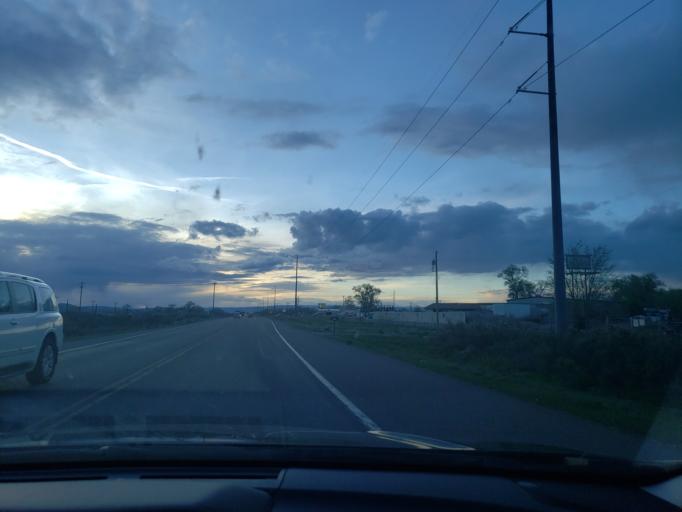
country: US
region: Colorado
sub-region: Mesa County
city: Redlands
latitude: 39.1185
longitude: -108.6613
